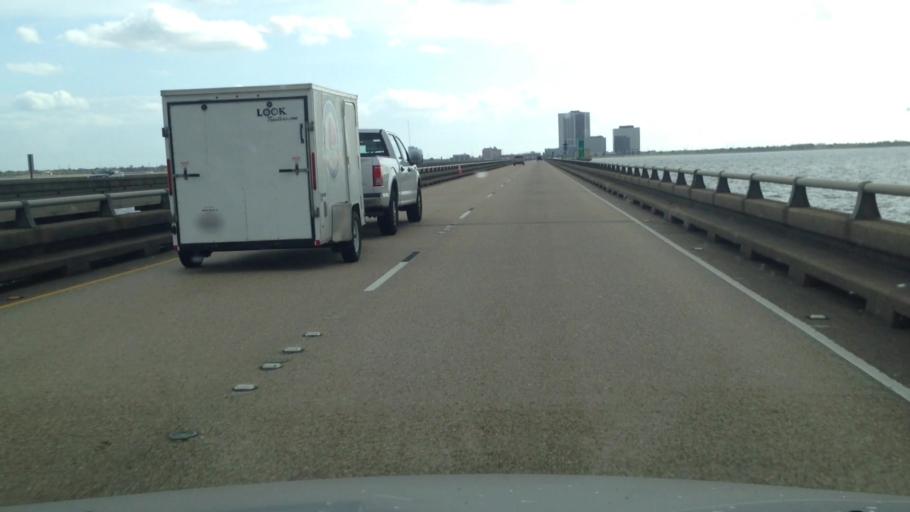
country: US
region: Louisiana
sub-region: Jefferson Parish
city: Metairie
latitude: 30.0410
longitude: -90.1507
